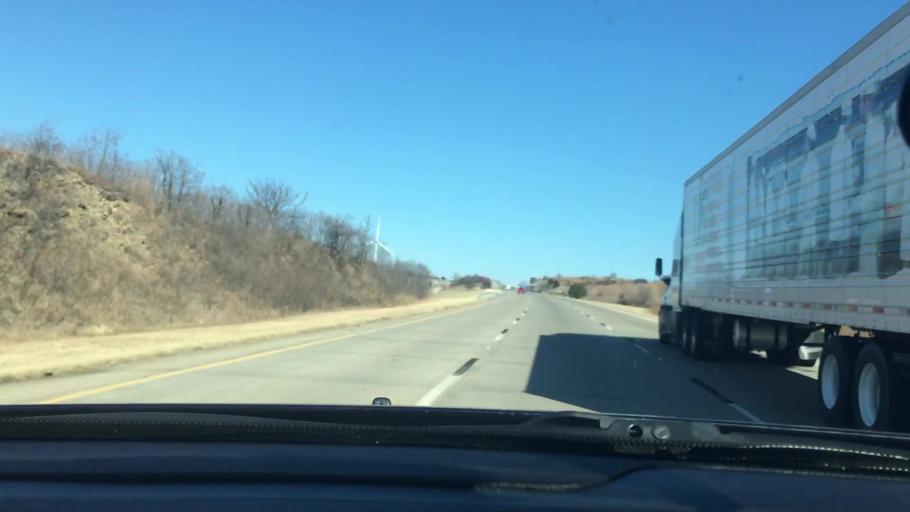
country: US
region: Oklahoma
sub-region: Murray County
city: Davis
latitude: 34.3638
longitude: -97.1469
